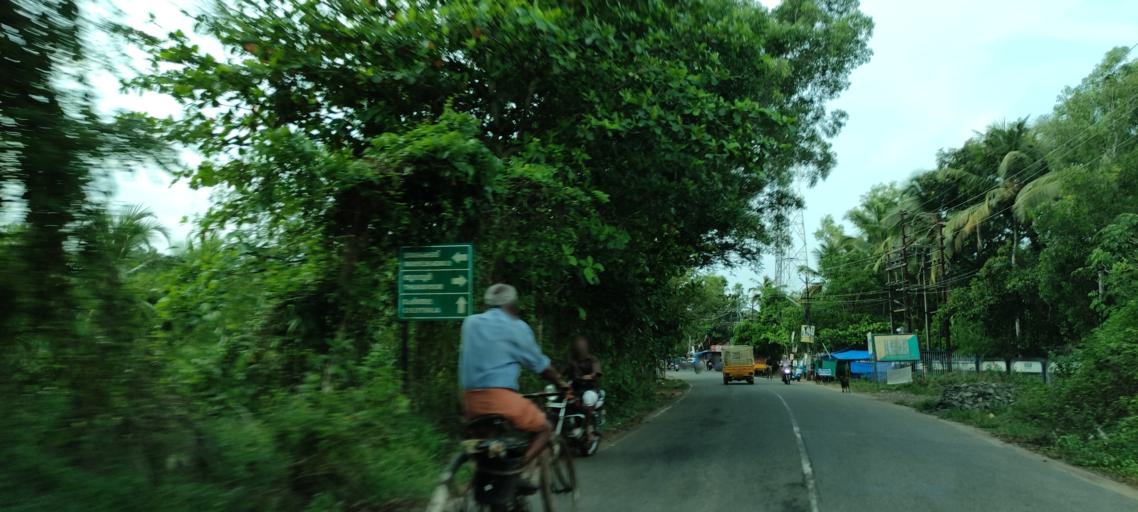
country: IN
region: Kerala
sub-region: Alappuzha
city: Kutiatodu
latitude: 9.7754
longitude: 76.3611
